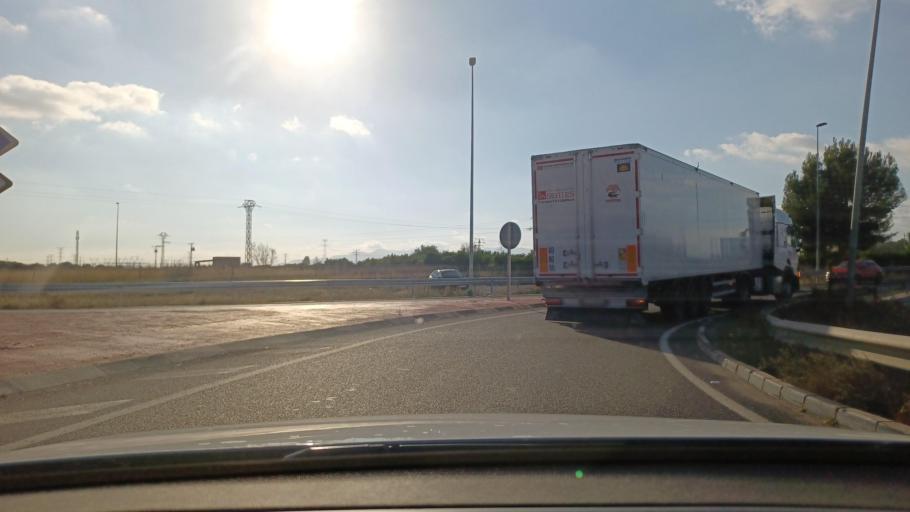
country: ES
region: Valencia
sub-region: Provincia de Castello
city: Vila-real
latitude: 39.9846
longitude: -0.0896
